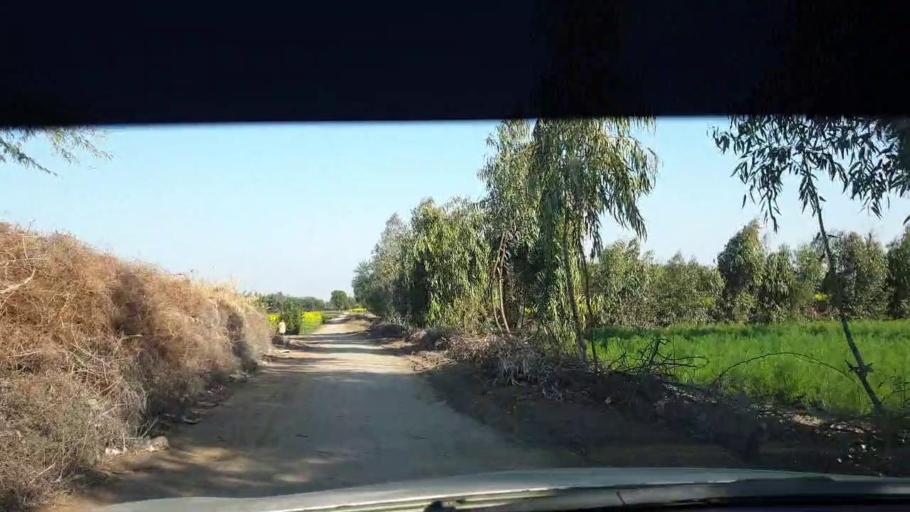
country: PK
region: Sindh
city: Berani
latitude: 25.7901
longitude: 68.9350
